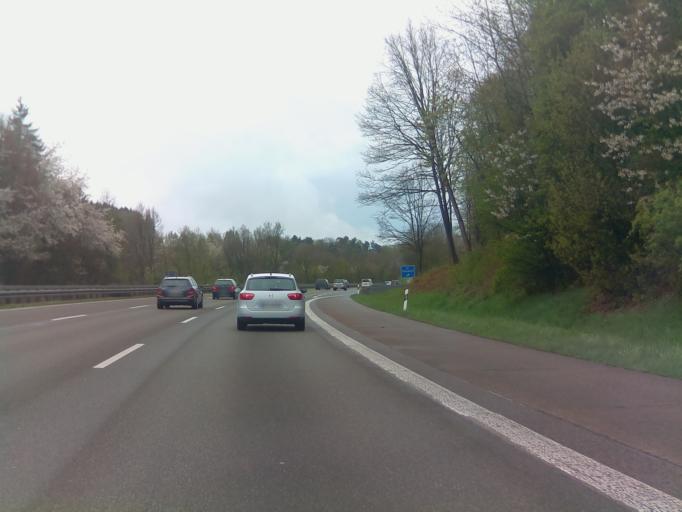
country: DE
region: Hesse
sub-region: Regierungsbezirk Kassel
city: Kirchheim
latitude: 50.7862
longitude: 9.5518
